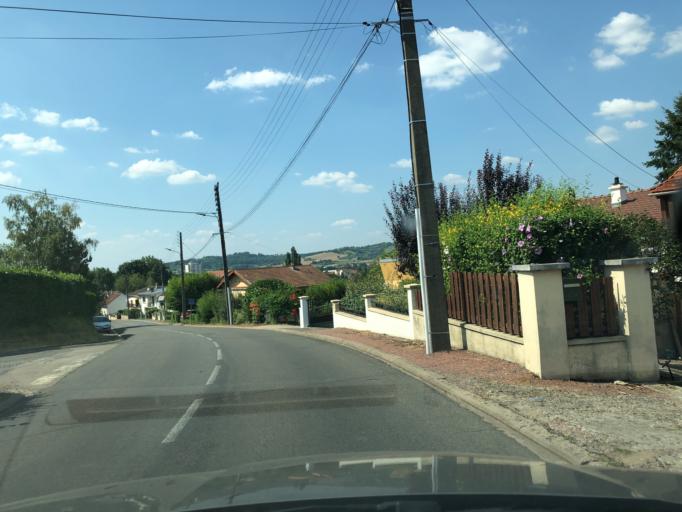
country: FR
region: Auvergne
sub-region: Departement de l'Allier
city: Cusset
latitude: 46.1262
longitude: 3.4668
